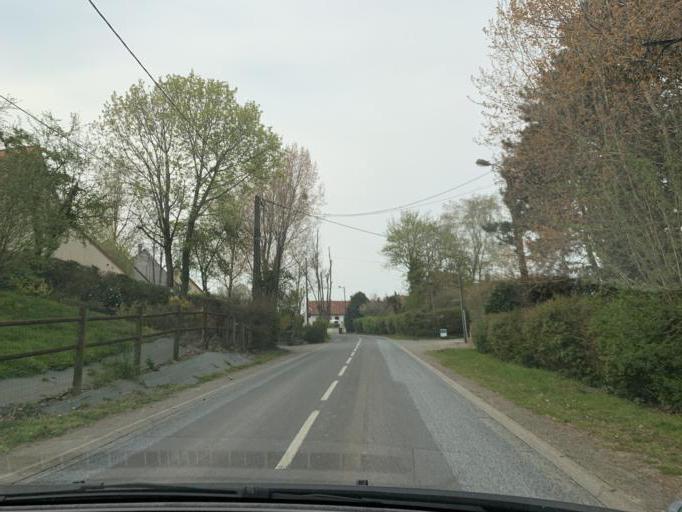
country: FR
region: Nord-Pas-de-Calais
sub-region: Departement du Pas-de-Calais
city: Longfosse
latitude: 50.7021
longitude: 1.7831
